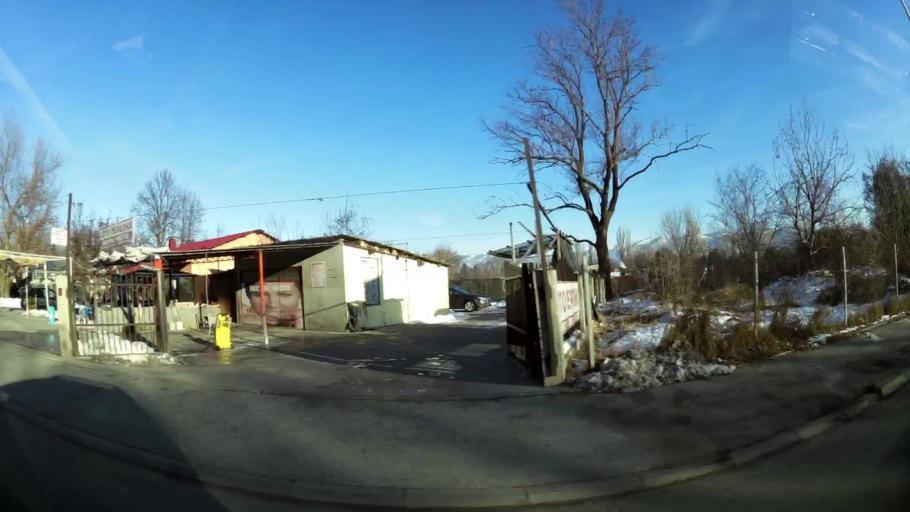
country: MK
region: Karpos
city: Skopje
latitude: 42.0069
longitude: 21.4100
